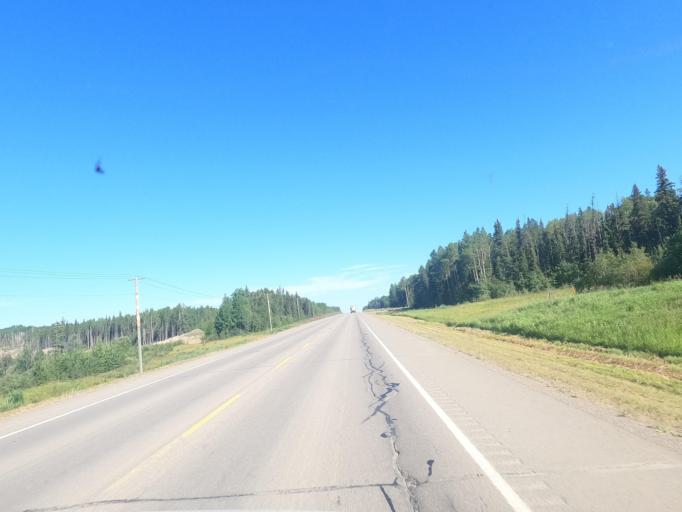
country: CA
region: British Columbia
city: Fort St. John
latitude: 56.6816
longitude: -121.6983
